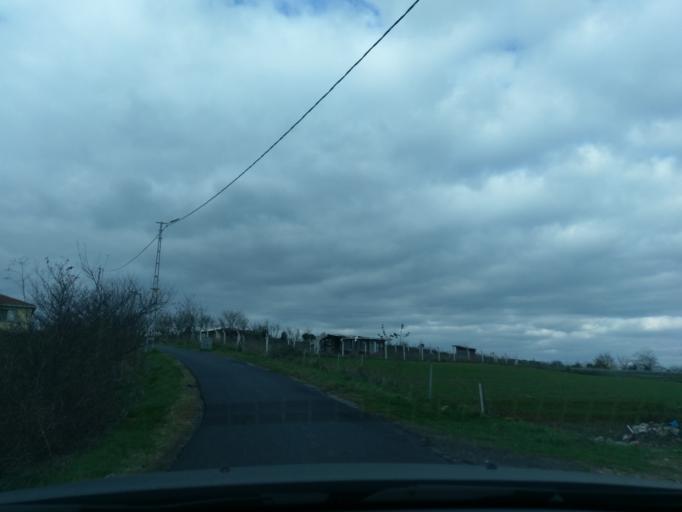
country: TR
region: Istanbul
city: Boyalik
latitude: 41.2735
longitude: 28.6590
